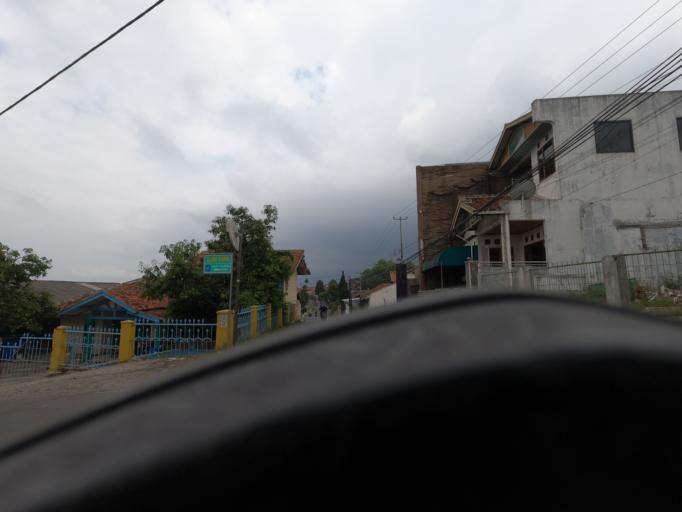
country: ID
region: West Java
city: Cimahi
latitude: -6.8161
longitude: 107.5490
